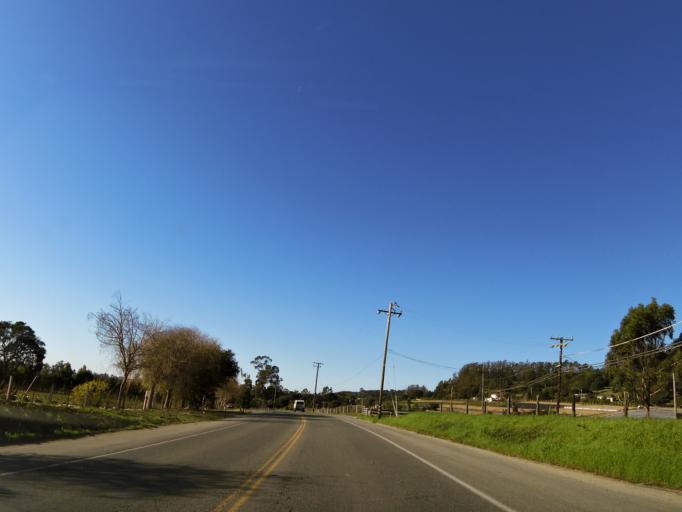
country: US
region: California
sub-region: Monterey County
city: Las Lomas
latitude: 36.8634
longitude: -121.7108
